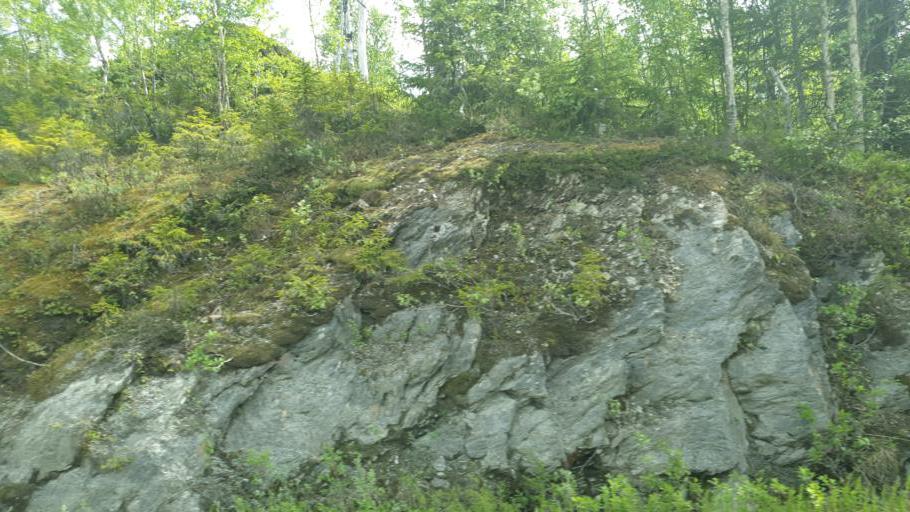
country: NO
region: Nord-Trondelag
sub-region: Leksvik
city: Leksvik
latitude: 63.6957
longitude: 10.4713
